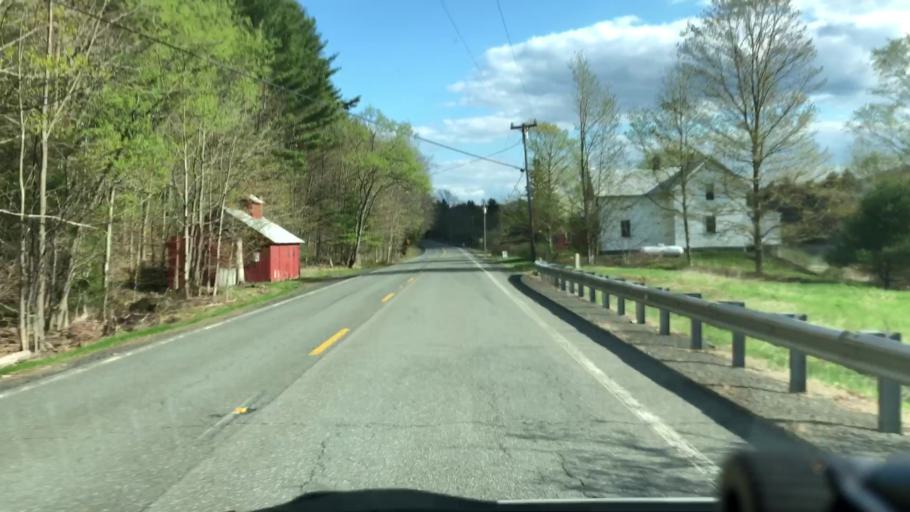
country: US
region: Massachusetts
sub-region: Hampshire County
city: Chesterfield
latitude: 42.3597
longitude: -72.9068
